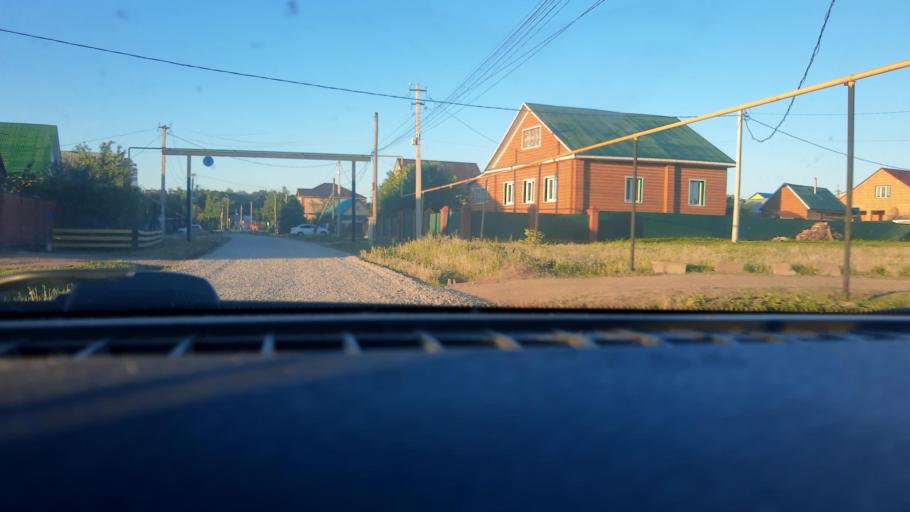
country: RU
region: Bashkortostan
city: Iglino
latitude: 54.8233
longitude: 56.3817
